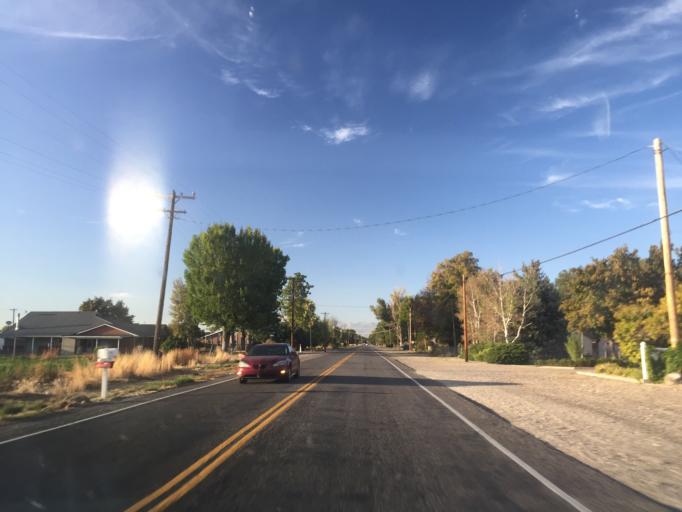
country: US
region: Utah
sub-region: Utah County
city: Benjamin
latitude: 40.0900
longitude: -111.7310
